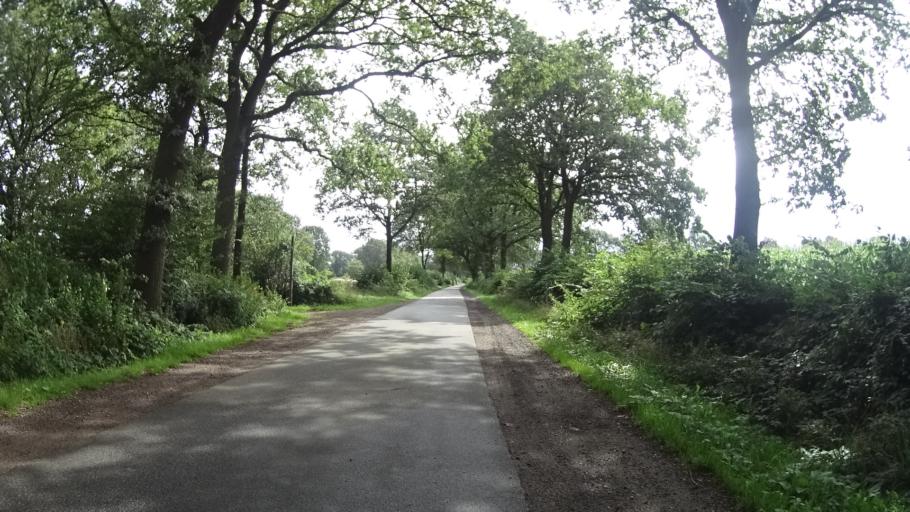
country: DE
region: Schleswig-Holstein
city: Tangstedt
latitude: 53.7577
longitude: 10.0347
